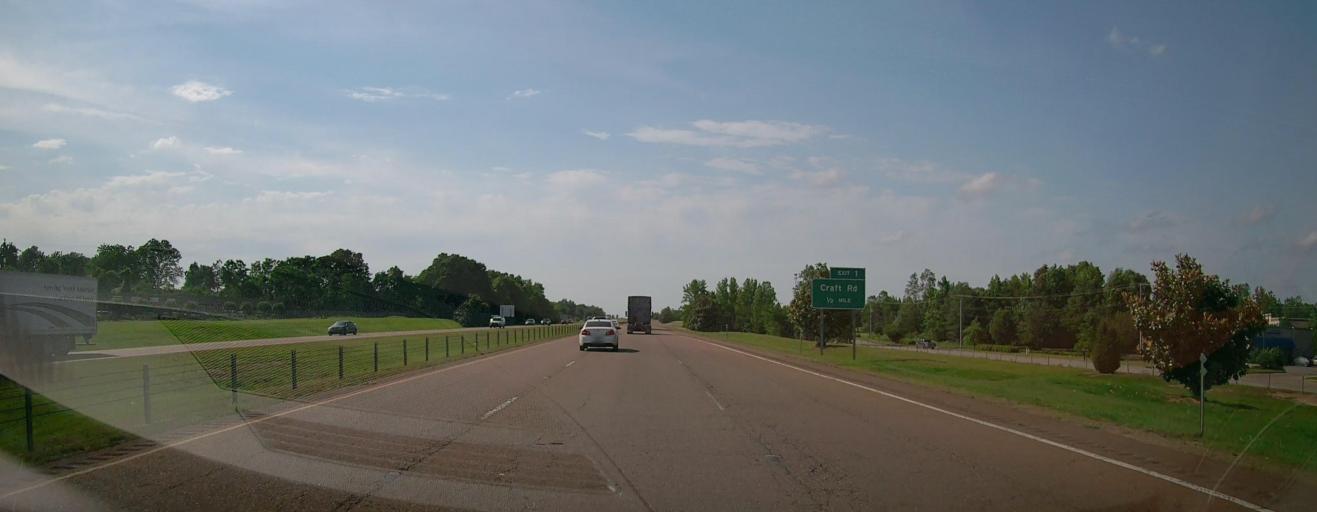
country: US
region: Mississippi
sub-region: De Soto County
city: Olive Branch
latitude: 34.9652
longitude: -89.8550
